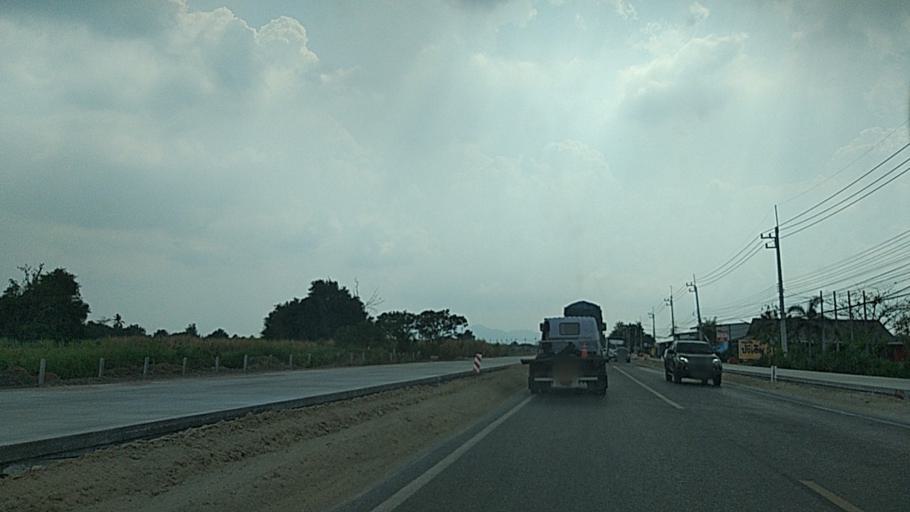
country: TH
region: Chon Buri
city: Ban Bueng
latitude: 13.3067
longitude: 101.1809
